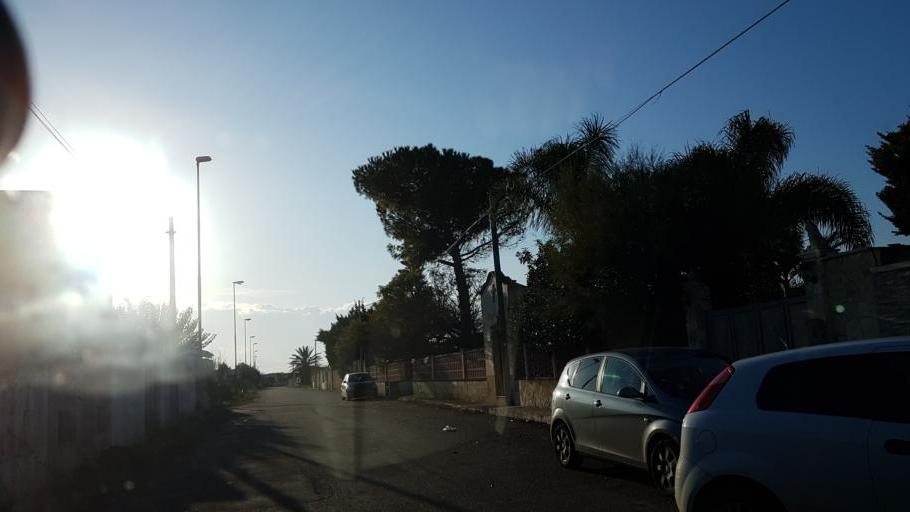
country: IT
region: Apulia
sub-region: Provincia di Brindisi
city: Torchiarolo
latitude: 40.5103
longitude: 18.0943
